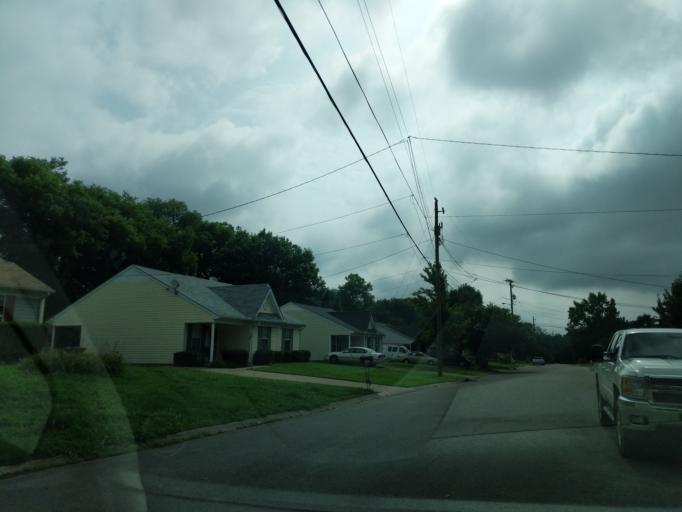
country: US
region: Tennessee
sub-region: Davidson County
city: Lakewood
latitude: 36.1774
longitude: -86.6237
